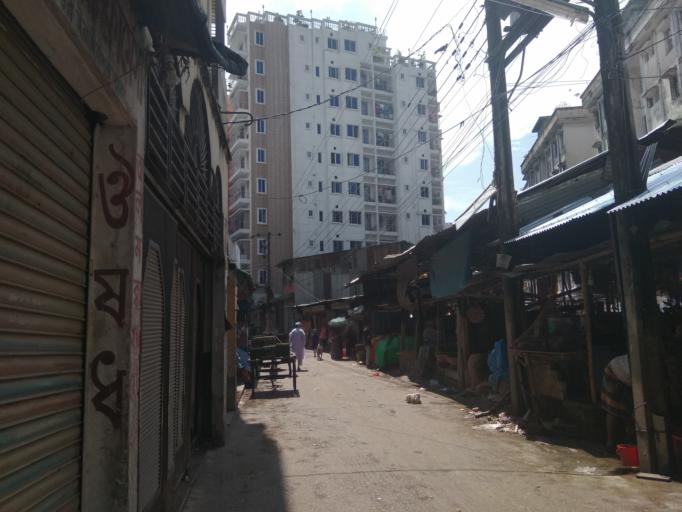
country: BD
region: Dhaka
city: Azimpur
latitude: 23.7993
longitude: 90.3817
